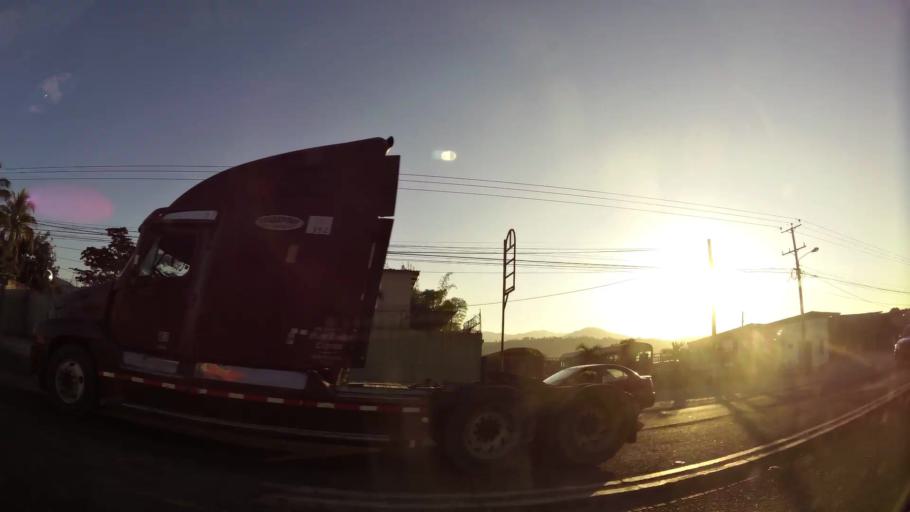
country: SV
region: La Libertad
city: Santa Tecla
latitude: 13.7274
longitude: -89.3776
